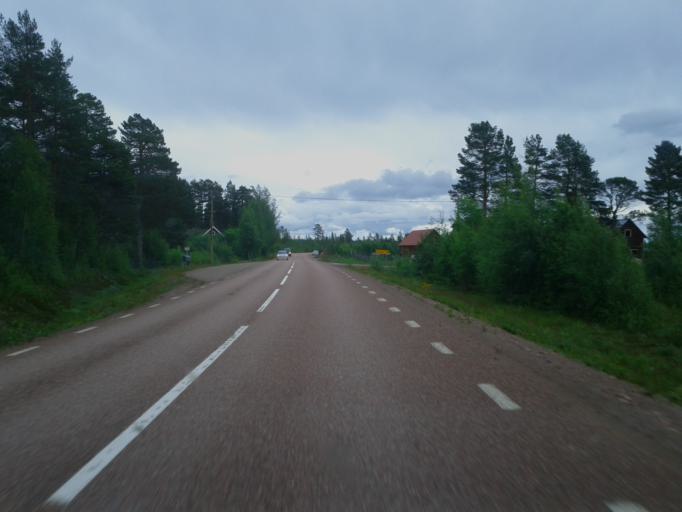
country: SE
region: Dalarna
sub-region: Alvdalens Kommun
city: AElvdalen
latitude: 61.5070
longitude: 13.3850
